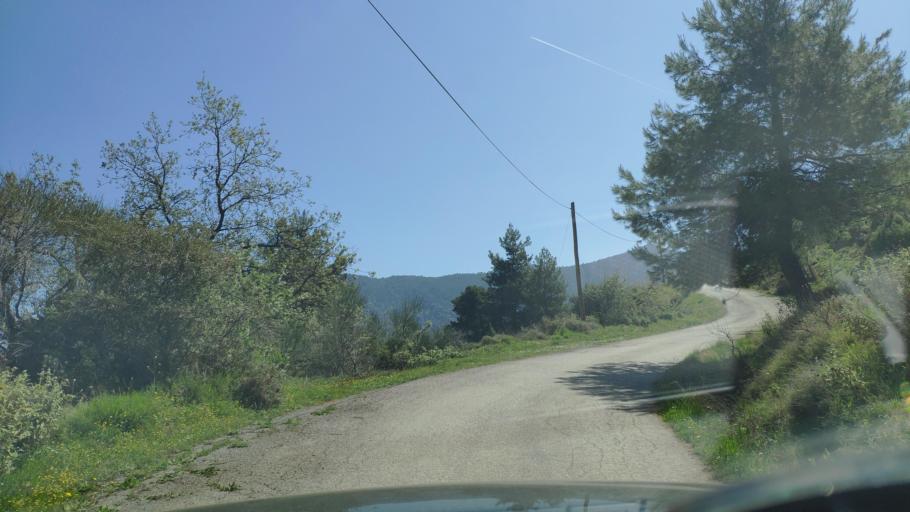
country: GR
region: West Greece
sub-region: Nomos Achaias
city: Akrata
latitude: 38.0813
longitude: 22.3224
